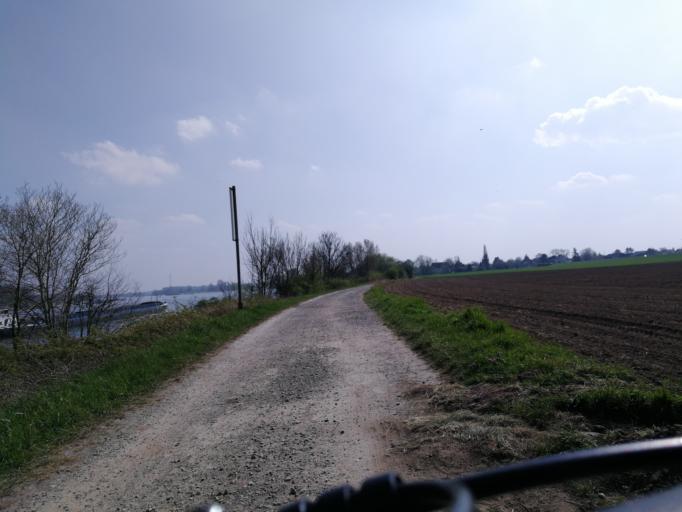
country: DE
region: North Rhine-Westphalia
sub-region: Regierungsbezirk Dusseldorf
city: Dormagen
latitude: 51.1350
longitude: 6.8459
